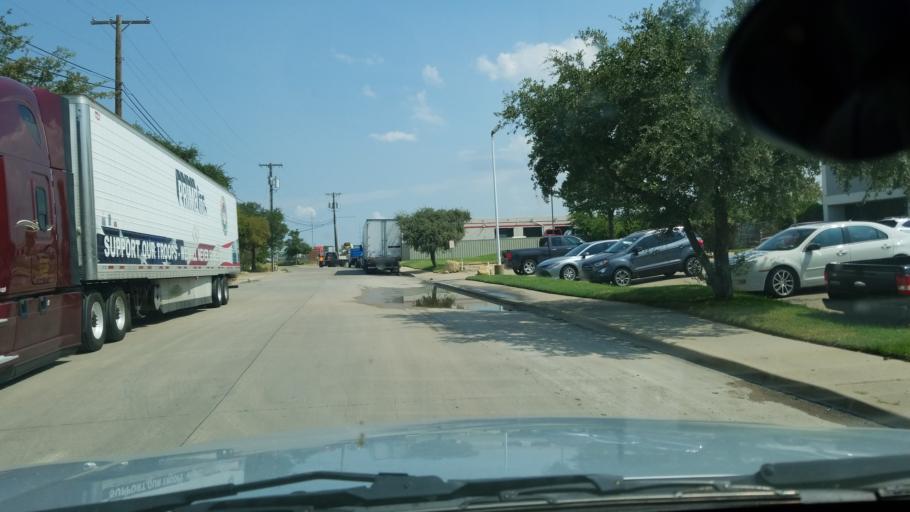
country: US
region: Texas
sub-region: Dallas County
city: Farmers Branch
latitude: 32.8671
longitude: -96.9048
